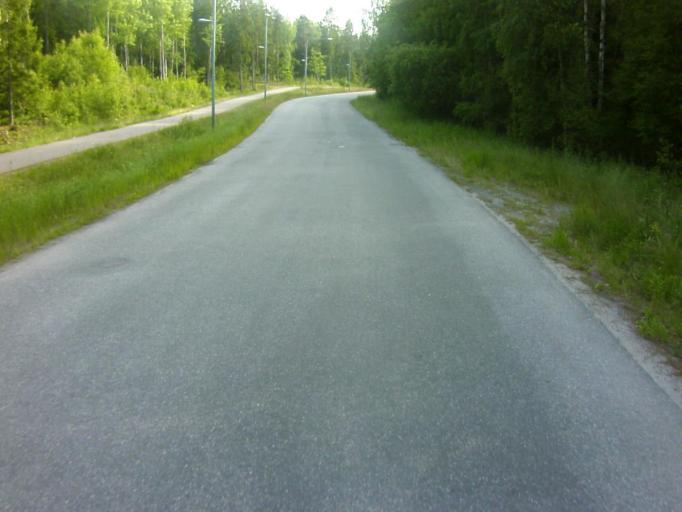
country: SE
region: Soedermanland
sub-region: Eskilstuna Kommun
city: Eskilstuna
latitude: 59.3532
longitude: 16.5125
